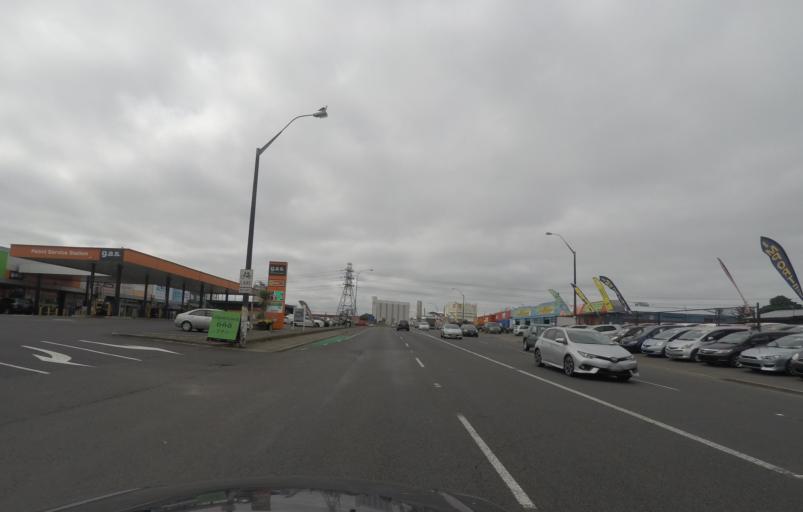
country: NZ
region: Auckland
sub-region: Auckland
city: Wiri
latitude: -36.9554
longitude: 174.8501
